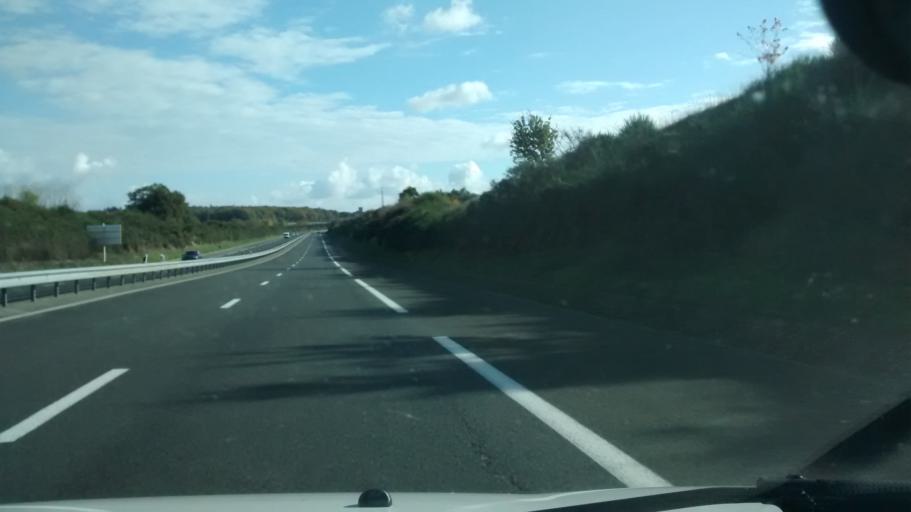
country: FR
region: Pays de la Loire
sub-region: Departement de Maine-et-Loire
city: Noyant-la-Gravoyere
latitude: 47.7085
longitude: -0.9626
